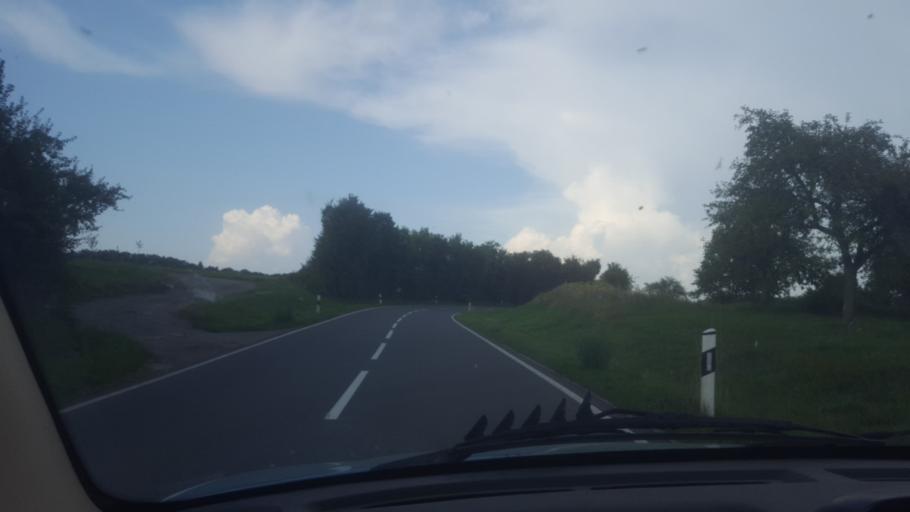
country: DE
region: Baden-Wuerttemberg
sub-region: Regierungsbezirk Stuttgart
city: Niederstetten
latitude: 49.4290
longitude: 9.8924
